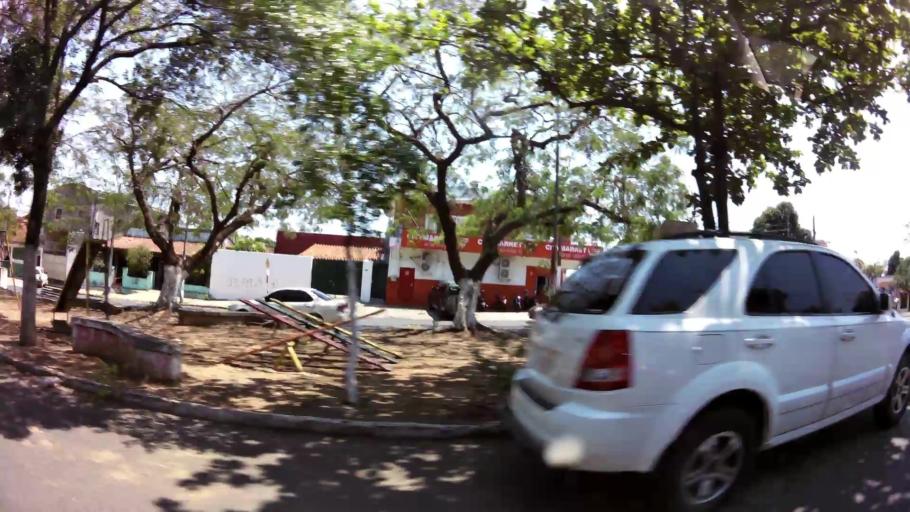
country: PY
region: Asuncion
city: Asuncion
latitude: -25.3075
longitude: -57.6403
